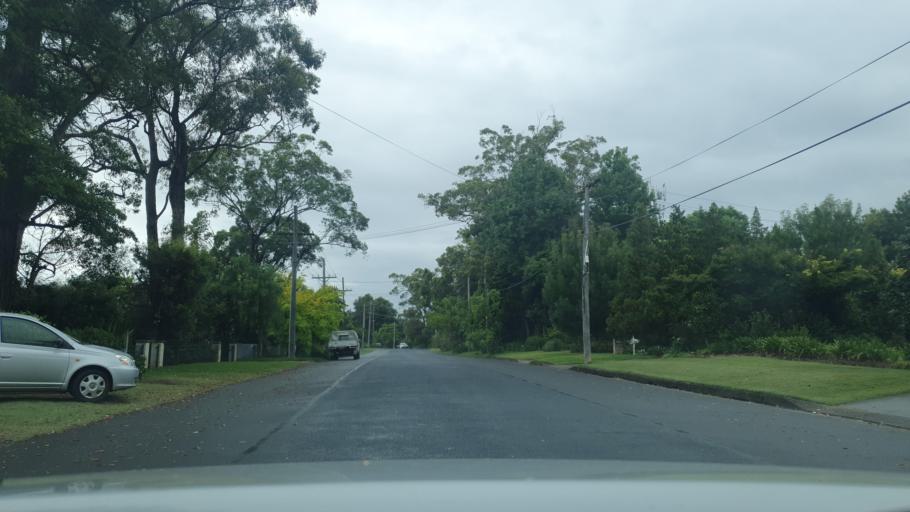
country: AU
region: New South Wales
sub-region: Blue Mountains Municipality
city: Glenbrook
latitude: -33.7737
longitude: 150.6286
